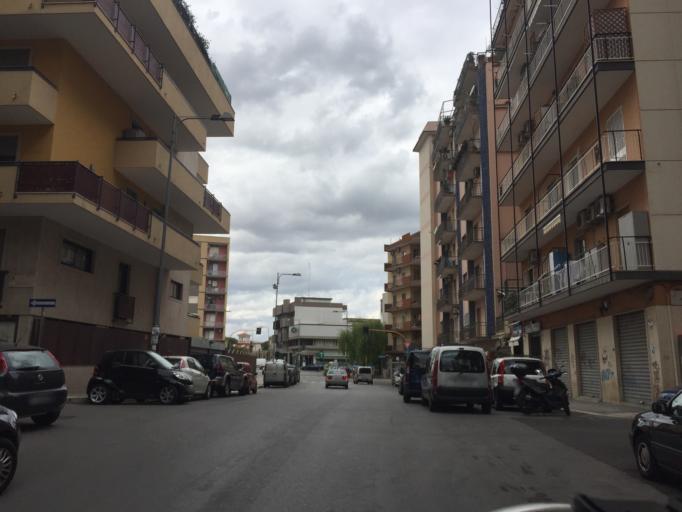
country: IT
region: Apulia
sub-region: Provincia di Bari
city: Bari
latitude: 41.1149
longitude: 16.8632
